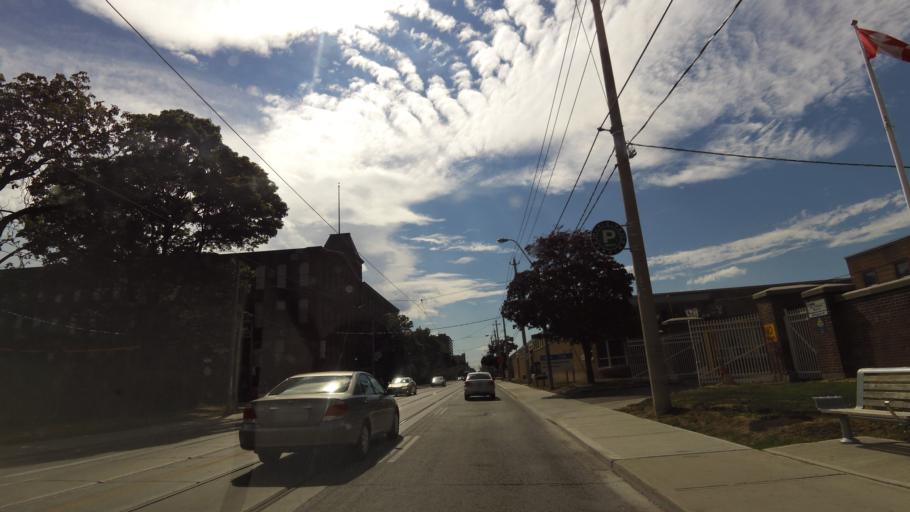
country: CA
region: Ontario
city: Toronto
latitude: 43.6396
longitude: -79.4243
